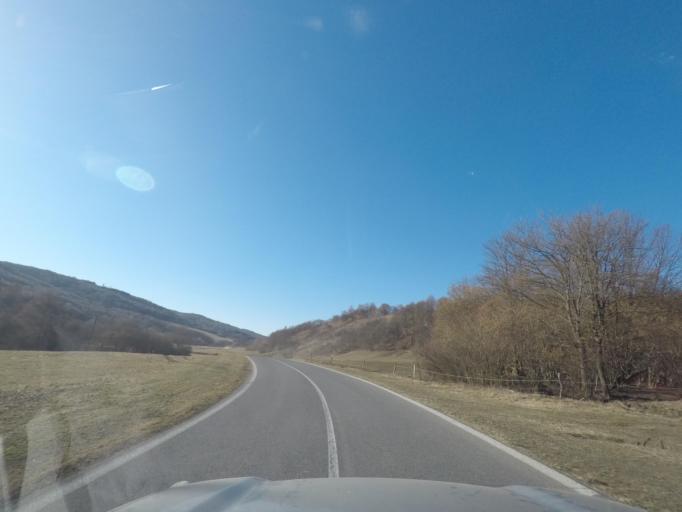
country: SK
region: Presovsky
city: Medzilaborce
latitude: 49.1776
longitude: 22.0237
